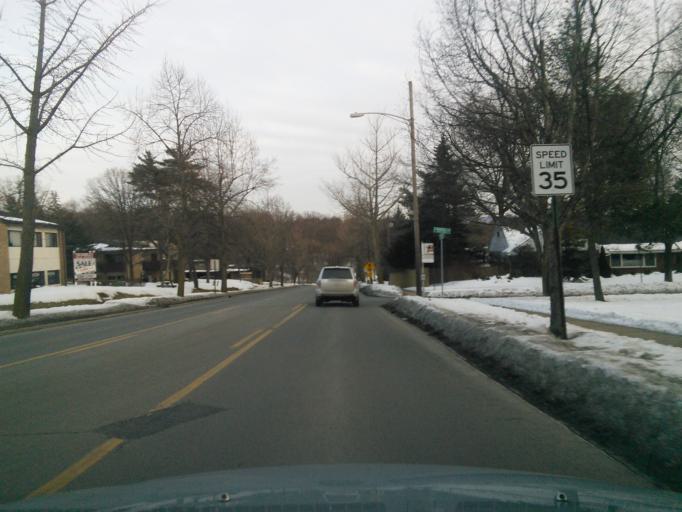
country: US
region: Pennsylvania
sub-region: Centre County
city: State College
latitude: 40.7977
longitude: -77.8454
